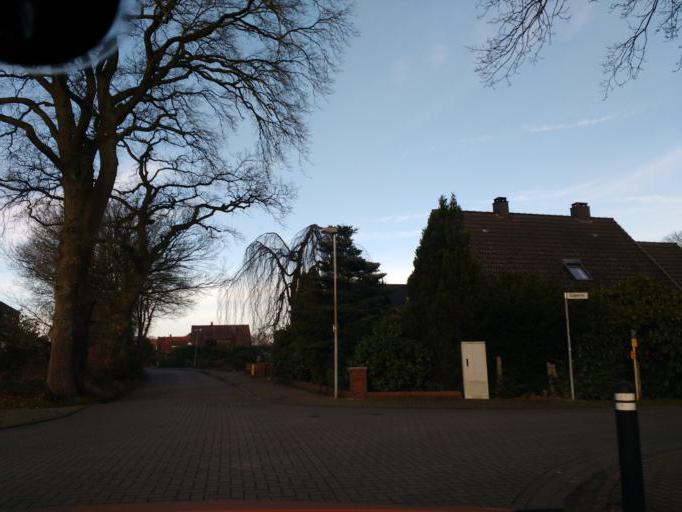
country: DE
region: Lower Saxony
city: Hude
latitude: 53.1181
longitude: 8.4606
